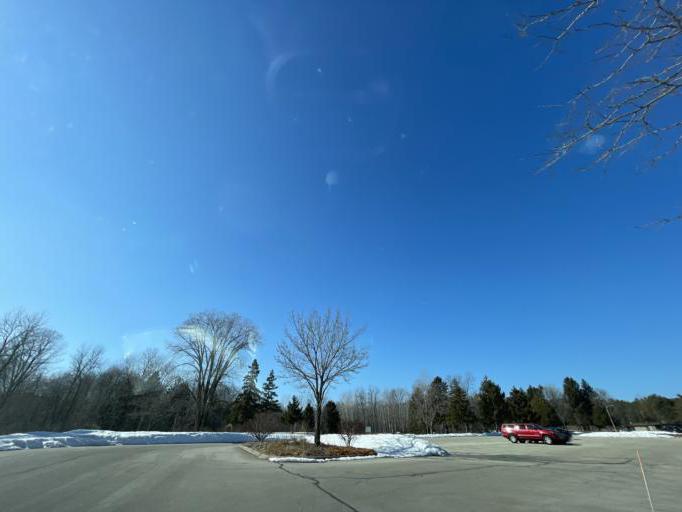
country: US
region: Wisconsin
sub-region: Brown County
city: Suamico
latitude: 44.6600
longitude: -88.0907
